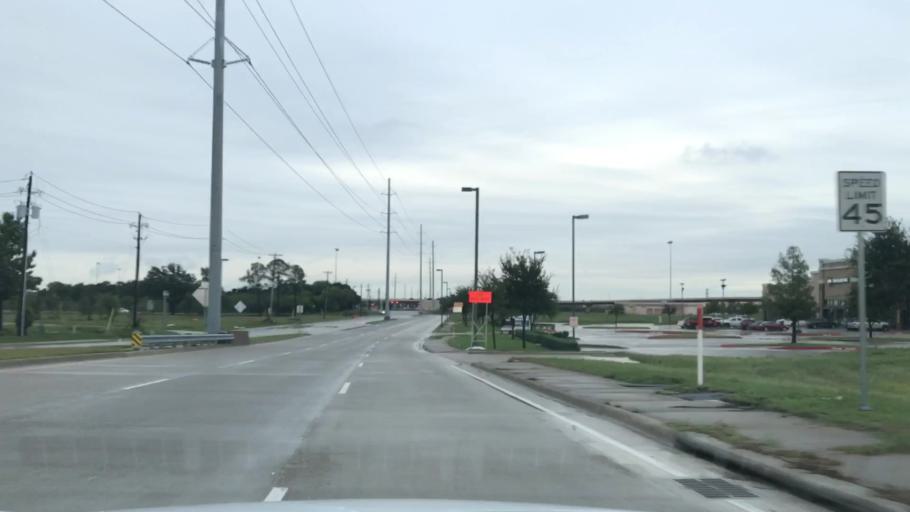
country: US
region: Texas
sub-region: Dallas County
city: Coppell
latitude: 32.9727
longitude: -97.0359
